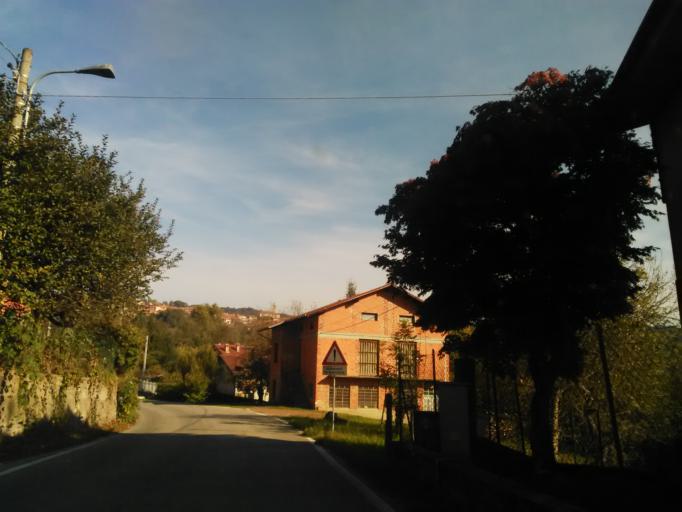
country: IT
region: Piedmont
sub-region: Provincia di Biella
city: Crevacuore
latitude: 45.6928
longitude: 8.2472
